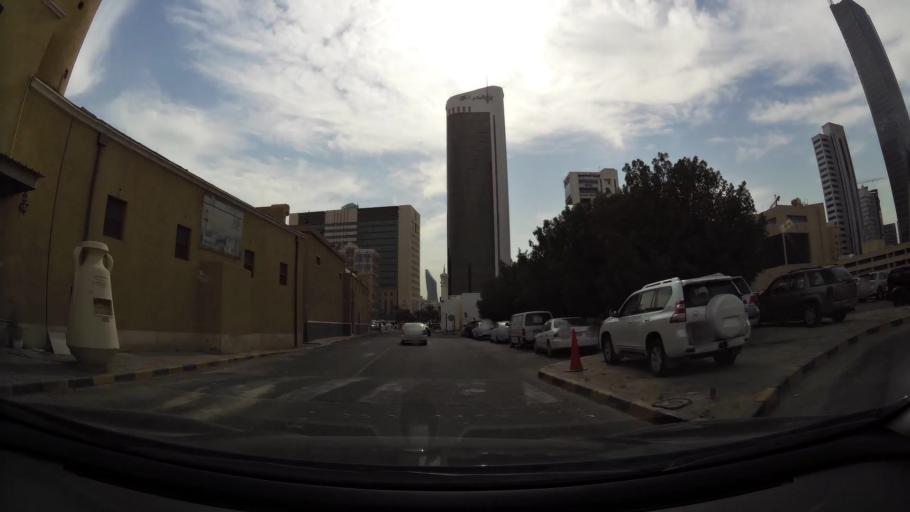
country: KW
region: Al Asimah
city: Kuwait City
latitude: 29.3799
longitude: 47.9786
